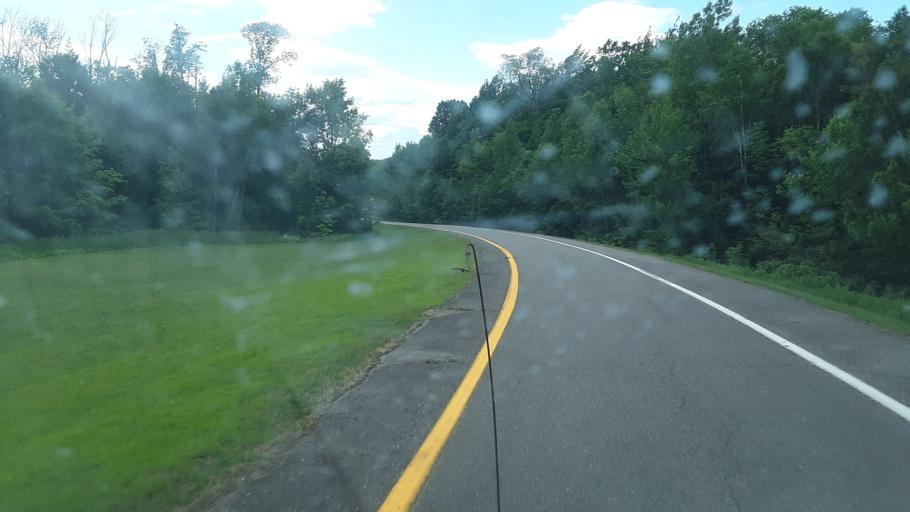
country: US
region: Maine
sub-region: Penobscot County
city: Medway
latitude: 45.7147
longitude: -68.4729
